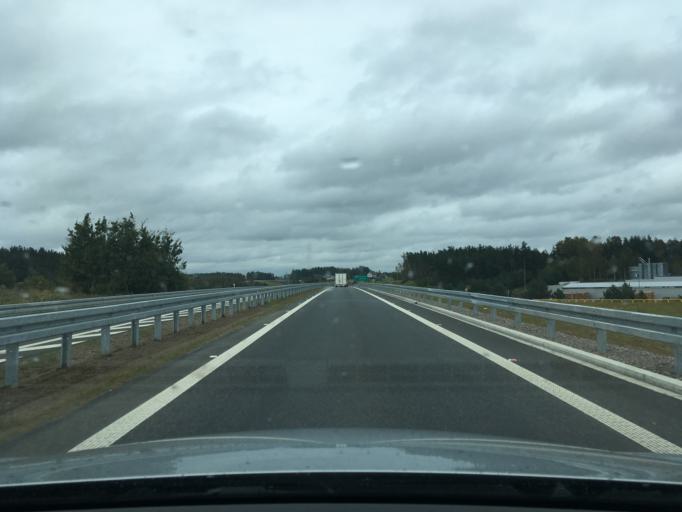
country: PL
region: Pomeranian Voivodeship
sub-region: Powiat koscierski
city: Koscierzyna
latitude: 54.1148
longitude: 18.0092
